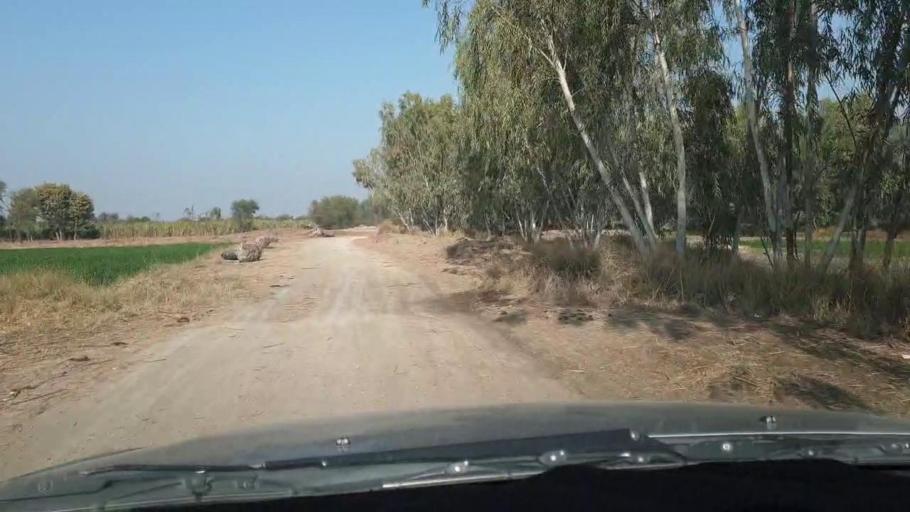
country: PK
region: Sindh
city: Mirpur Mathelo
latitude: 27.9194
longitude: 69.5567
